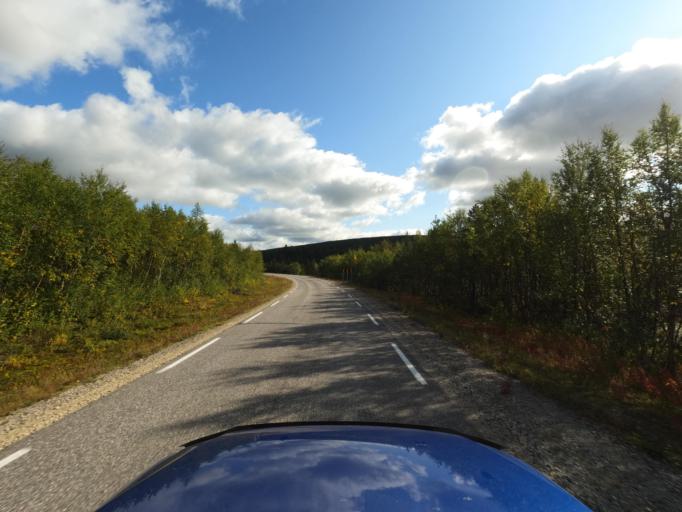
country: NO
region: Finnmark Fylke
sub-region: Karasjok
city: Karasjohka
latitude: 69.4272
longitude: 24.9399
